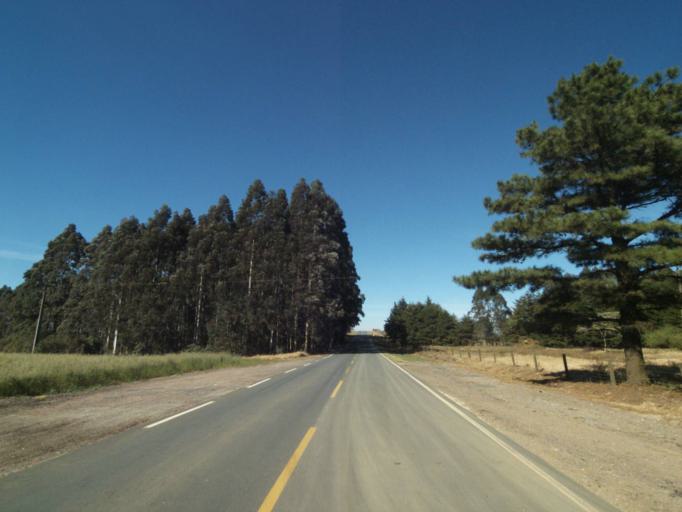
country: BR
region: Parana
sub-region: Castro
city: Castro
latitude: -24.7150
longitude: -50.1914
